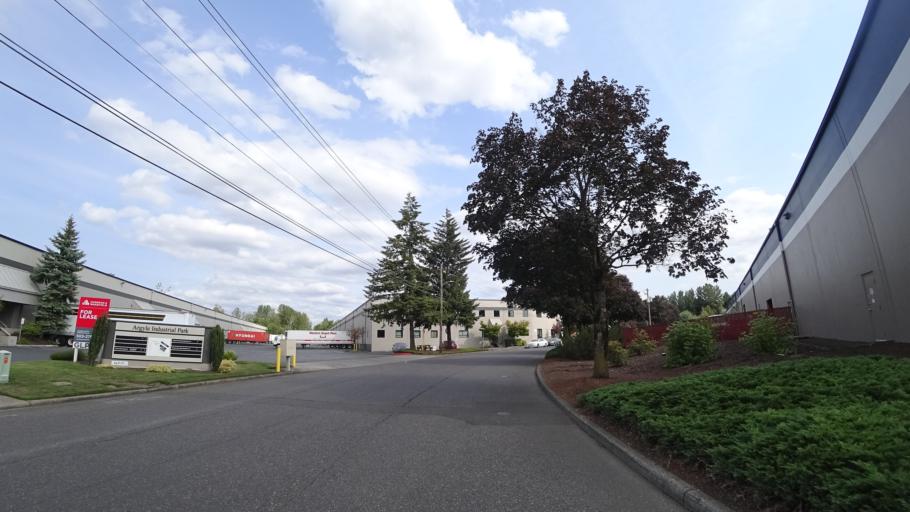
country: US
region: Washington
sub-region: Clark County
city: Vancouver
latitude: 45.5794
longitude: -122.6421
